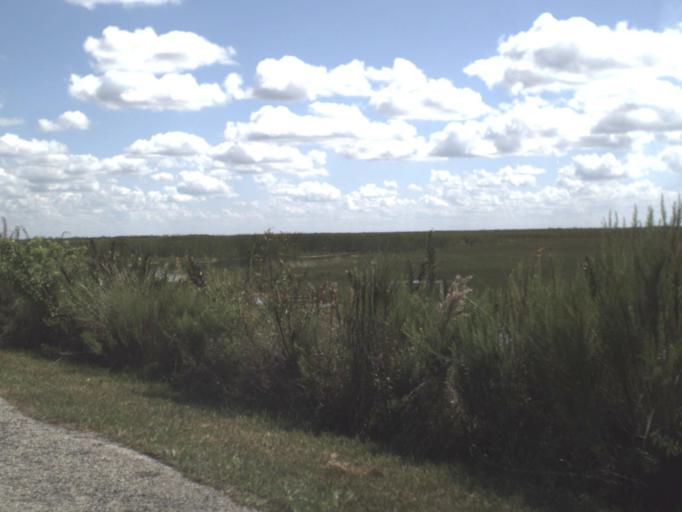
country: US
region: Florida
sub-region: Collier County
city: Marco
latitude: 25.9236
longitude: -81.4172
